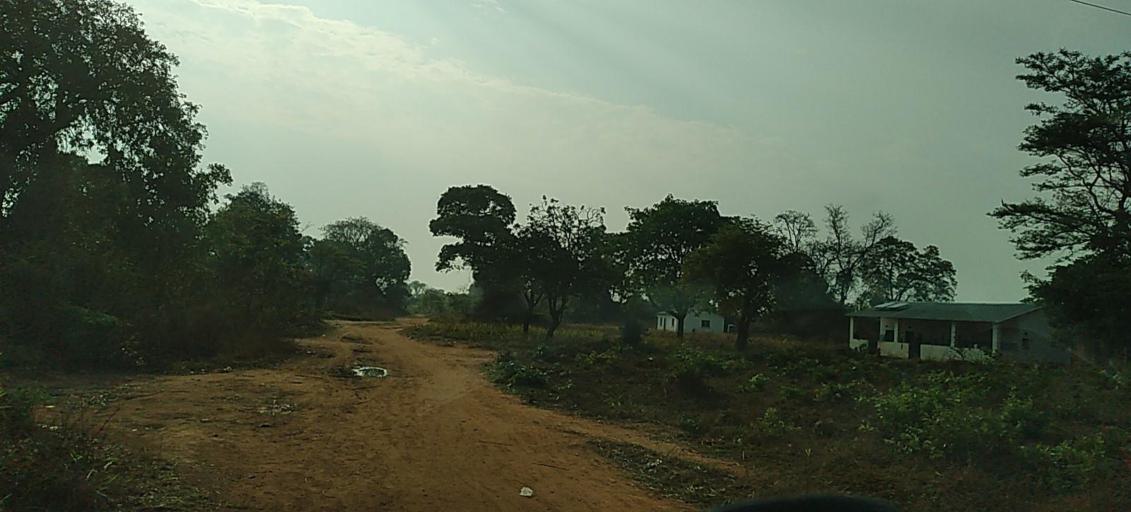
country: ZM
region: North-Western
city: Solwezi
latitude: -12.3530
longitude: 26.5318
